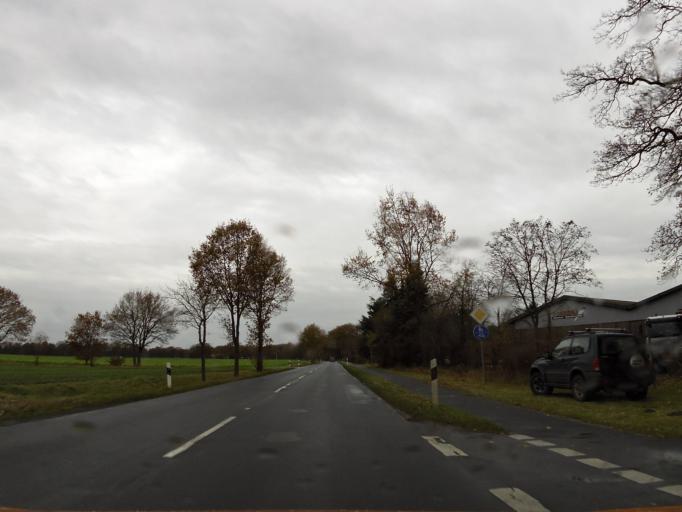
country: DE
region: Lower Saxony
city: Hude
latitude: 53.0886
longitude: 8.4576
